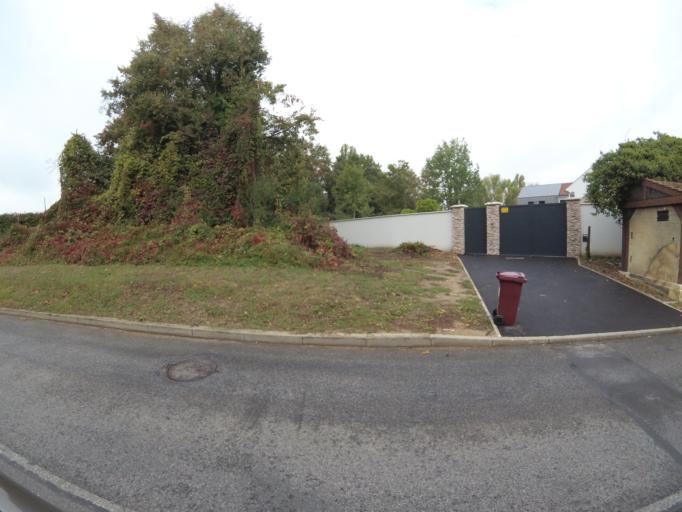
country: FR
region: Ile-de-France
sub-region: Departement de Seine-et-Marne
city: Guermantes
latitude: 48.8538
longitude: 2.7039
